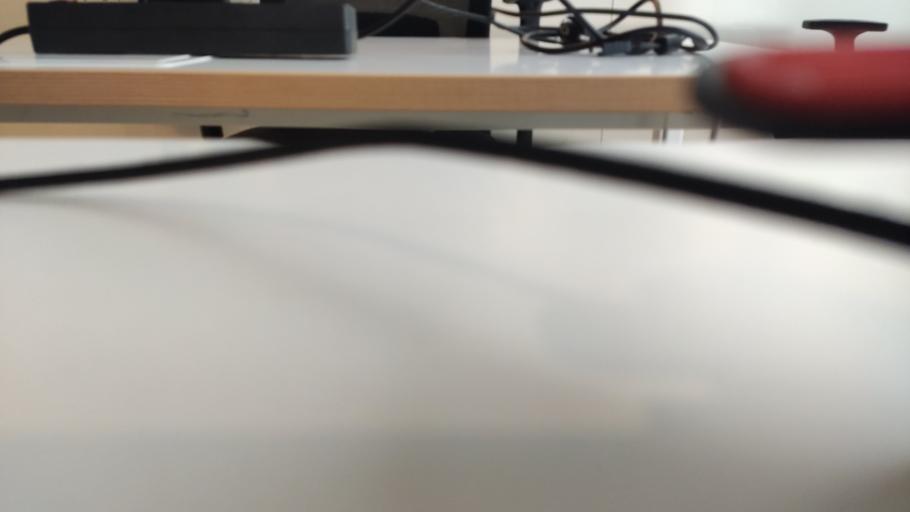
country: RU
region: Moskovskaya
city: Rogachevo
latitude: 56.4100
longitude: 37.0638
